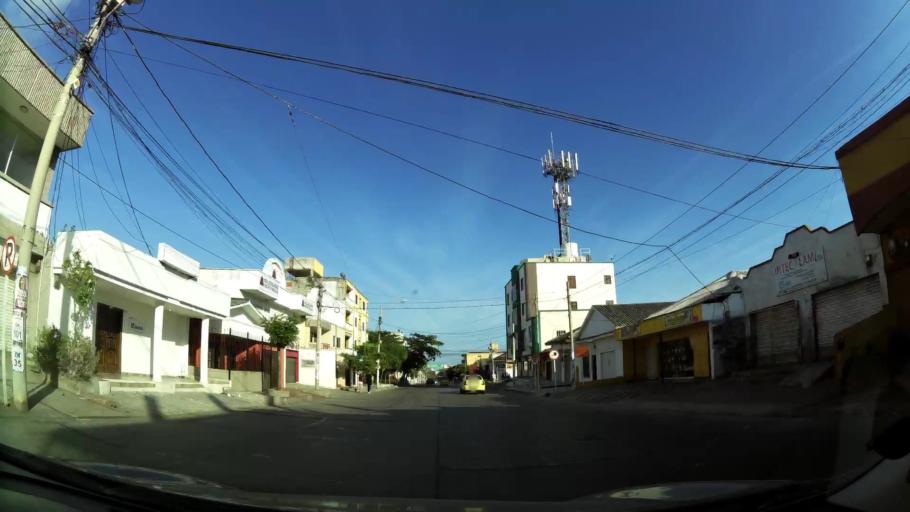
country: CO
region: Atlantico
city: Barranquilla
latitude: 10.9871
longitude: -74.7949
